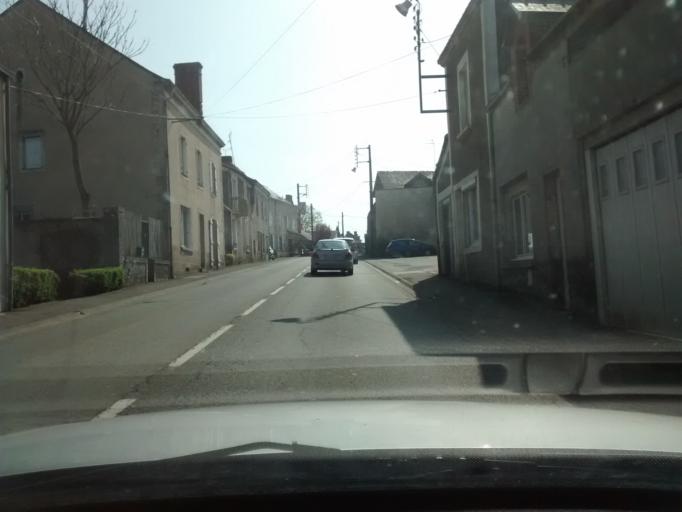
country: FR
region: Pays de la Loire
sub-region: Departement de la Mayenne
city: Soulge-sur-Ouette
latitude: 48.0599
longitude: -0.5694
